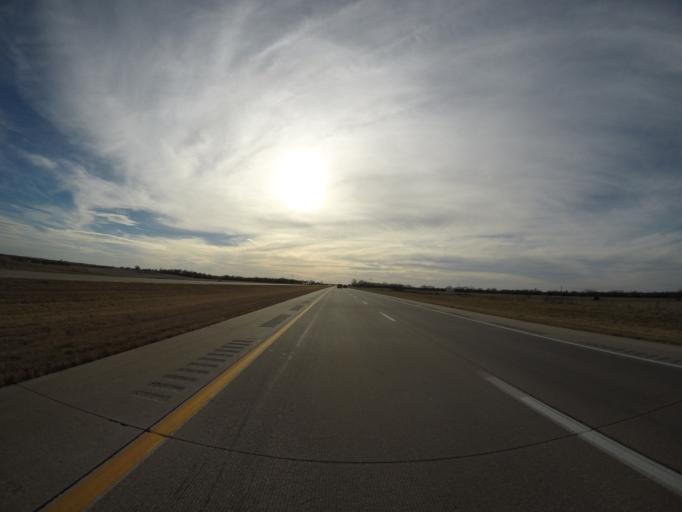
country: US
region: Kansas
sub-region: Johnson County
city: Edgerton
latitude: 38.7326
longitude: -95.0258
